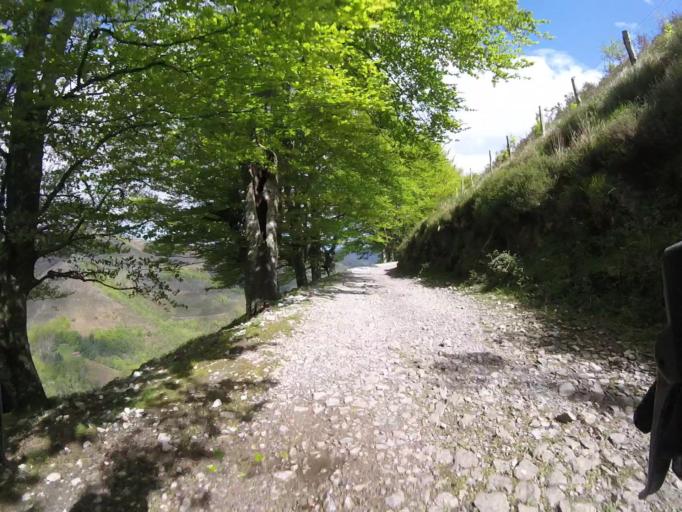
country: ES
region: Navarre
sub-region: Provincia de Navarra
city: Arano
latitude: 43.1823
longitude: -1.9005
